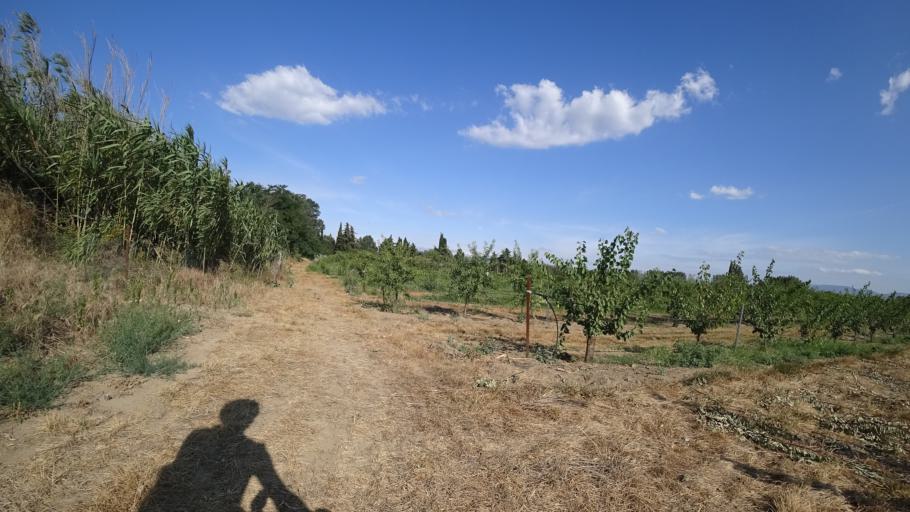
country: FR
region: Languedoc-Roussillon
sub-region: Departement des Pyrenees-Orientales
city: Rivesaltes
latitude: 42.7736
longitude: 2.8878
